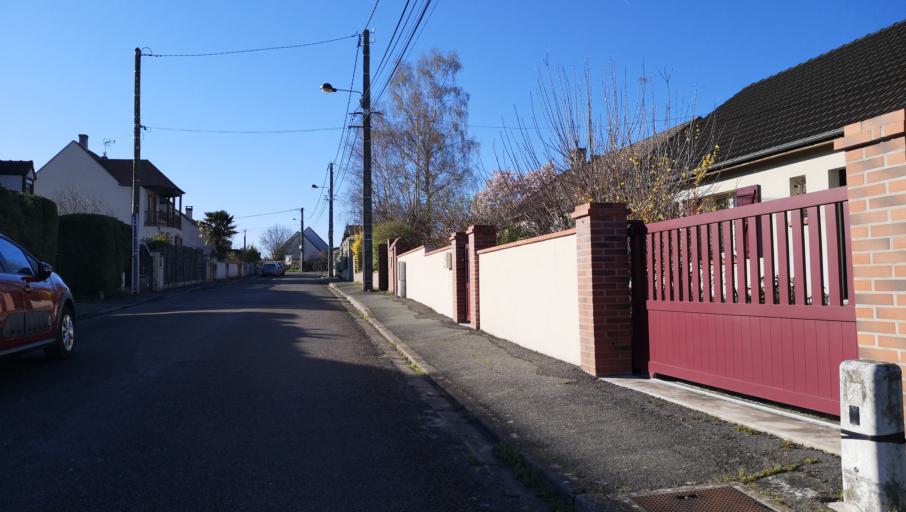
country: FR
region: Centre
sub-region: Departement du Loiret
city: Saint-Jean-de-Braye
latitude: 47.9077
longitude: 1.9899
